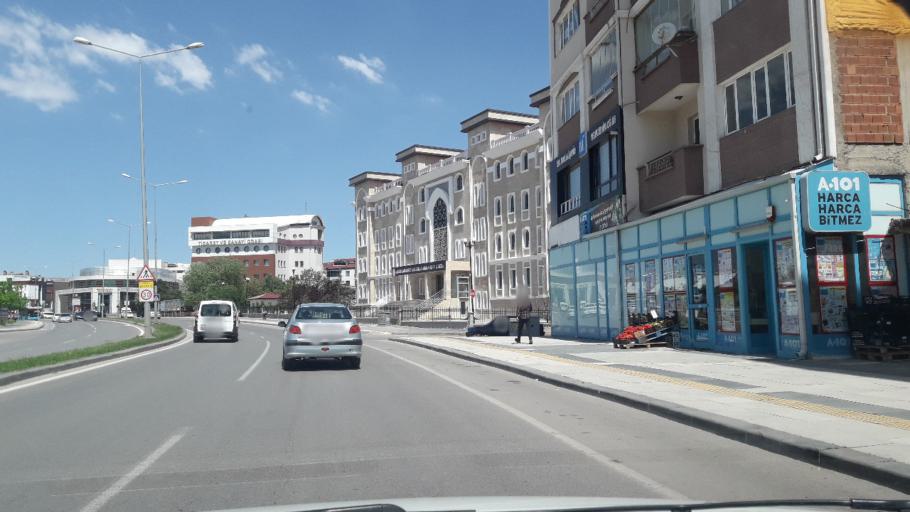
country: TR
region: Sivas
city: Sivas
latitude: 39.7408
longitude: 37.0148
